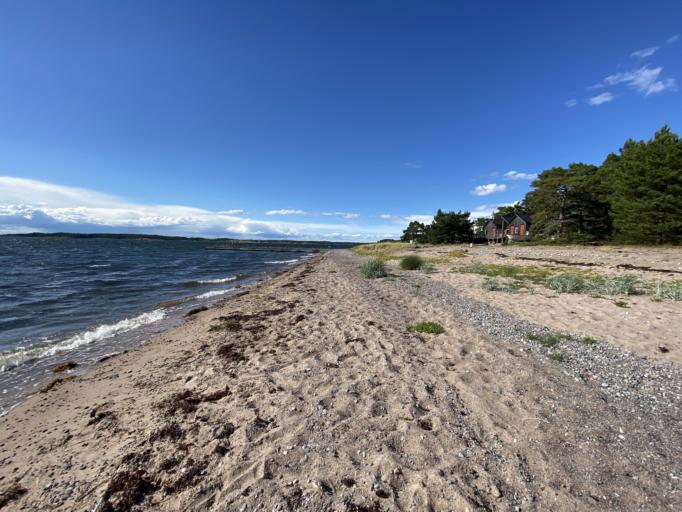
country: SE
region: Stockholm
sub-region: Varmdo Kommun
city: Holo
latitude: 59.2823
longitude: 18.9008
